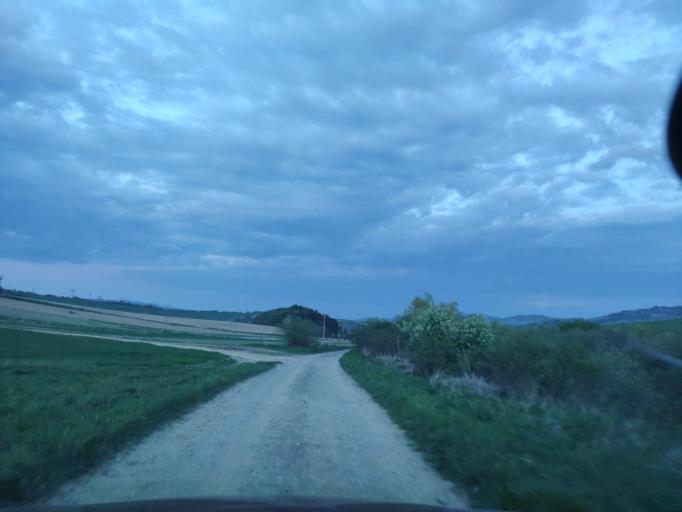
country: SK
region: Presovsky
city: Lipany
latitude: 49.1798
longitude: 20.8479
